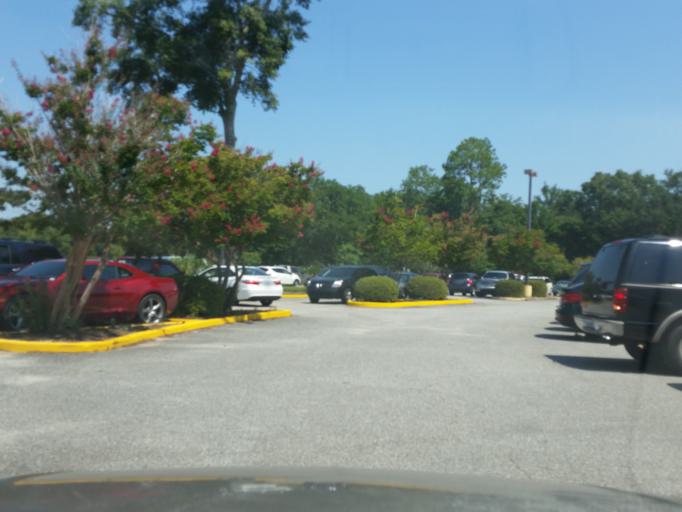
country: US
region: Florida
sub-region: Escambia County
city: Ferry Pass
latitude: 30.5129
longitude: -87.2221
